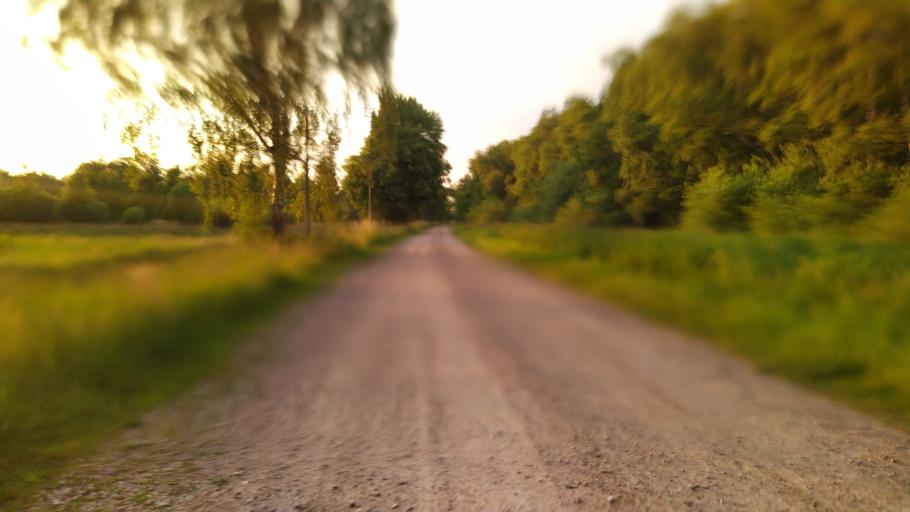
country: DE
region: Lower Saxony
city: Neu Wulmstorf
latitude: 53.4858
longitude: 9.8267
